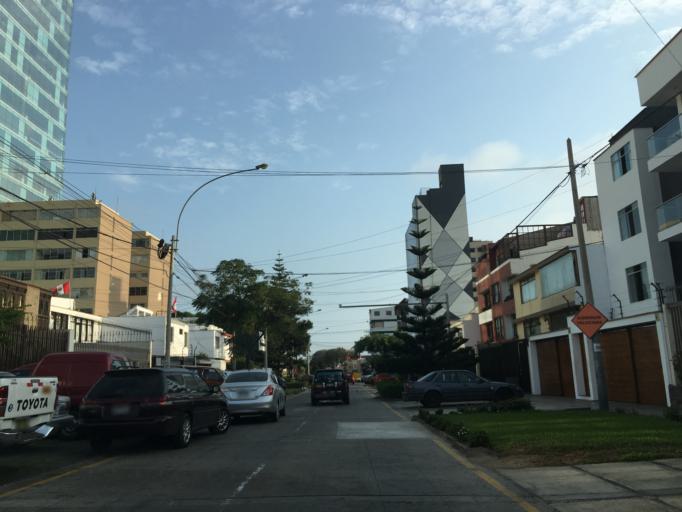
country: PE
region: Lima
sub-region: Lima
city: San Isidro
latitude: -12.0917
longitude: -77.0616
